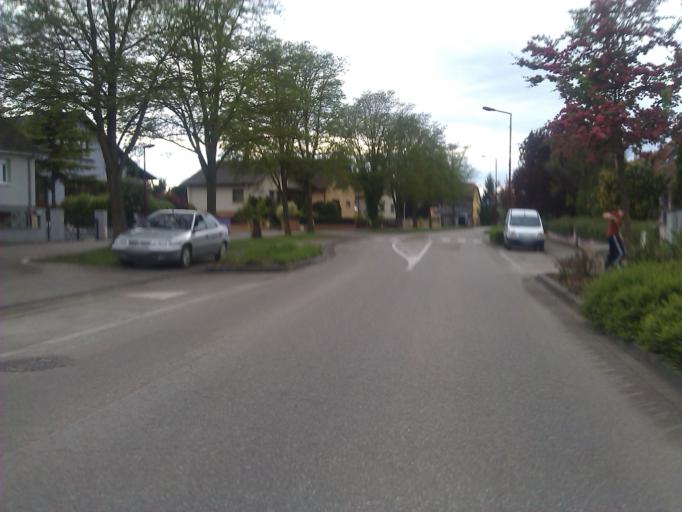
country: FR
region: Alsace
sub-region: Departement du Haut-Rhin
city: Jebsheim
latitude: 48.1616
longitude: 7.4948
